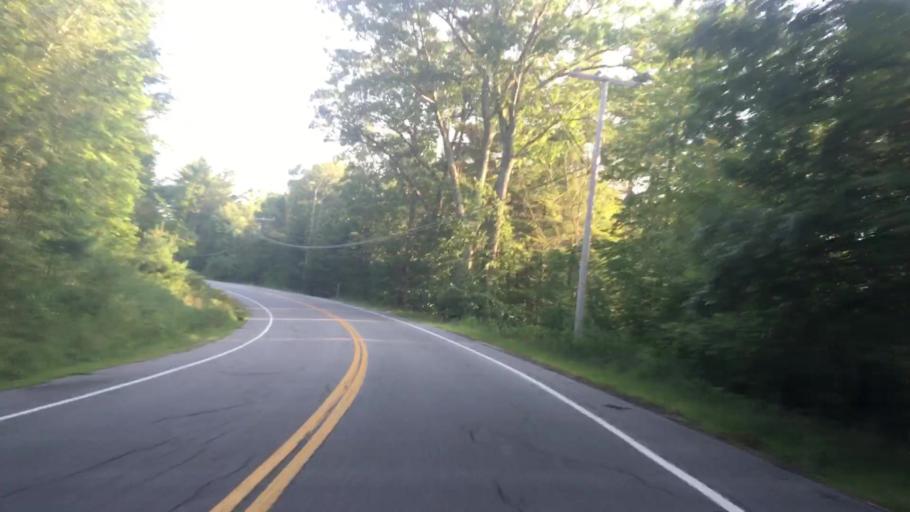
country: US
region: New Hampshire
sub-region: Belknap County
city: Gilmanton
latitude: 43.4562
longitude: -71.4216
